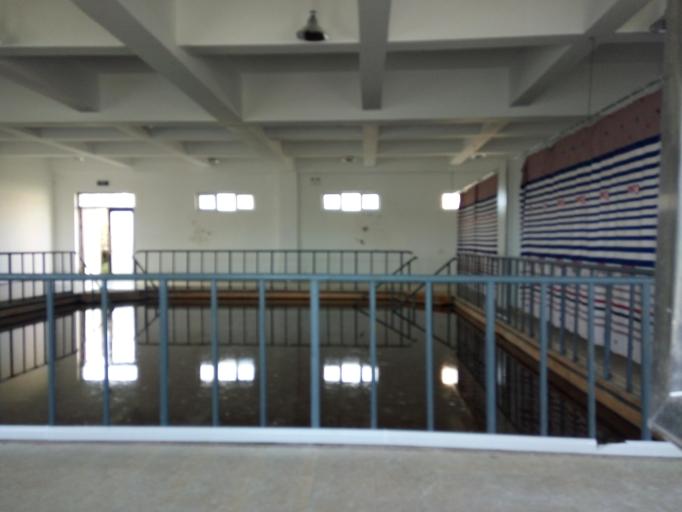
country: CN
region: Heilongjiang Sheng
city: Erjing
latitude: 48.6536
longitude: 126.1369
